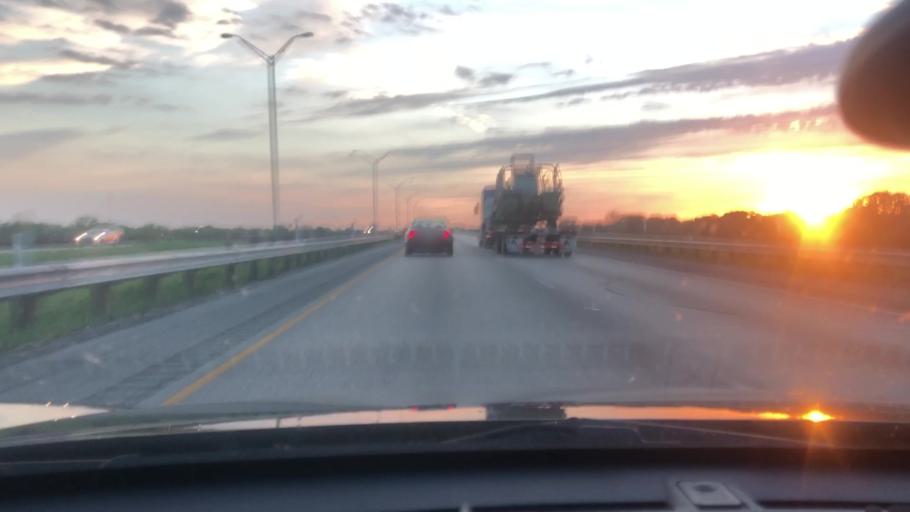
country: US
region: Texas
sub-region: Jackson County
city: Edna
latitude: 28.9865
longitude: -96.6514
